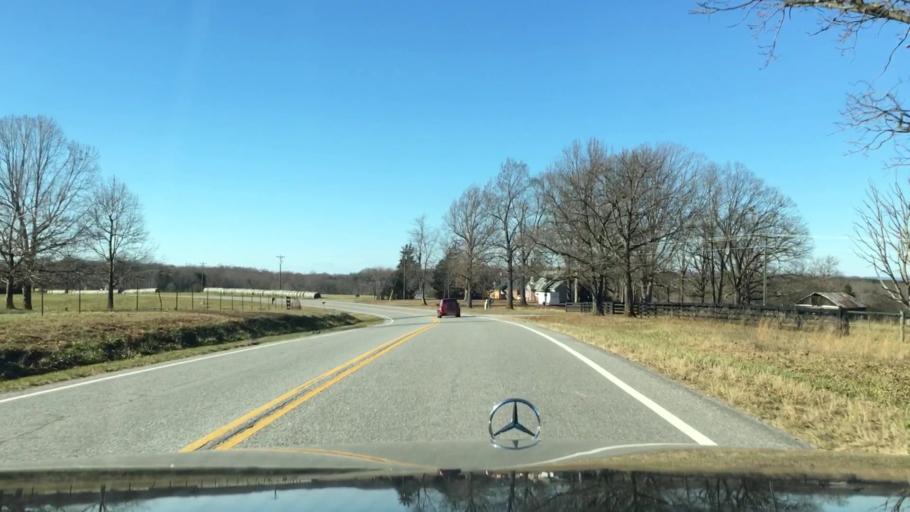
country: US
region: Virginia
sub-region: City of Bedford
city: Bedford
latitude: 37.2202
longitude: -79.4827
